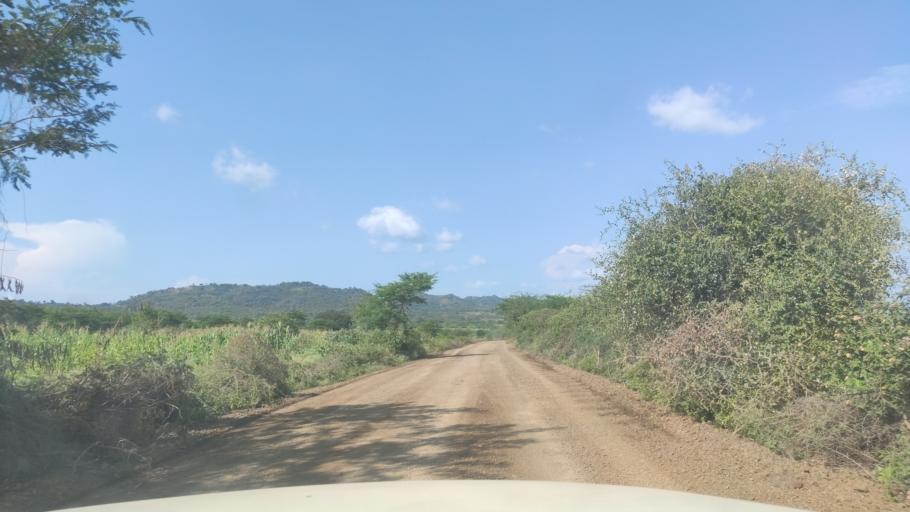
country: ET
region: Southern Nations, Nationalities, and People's Region
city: Felege Neway
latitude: 6.3842
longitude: 37.0948
